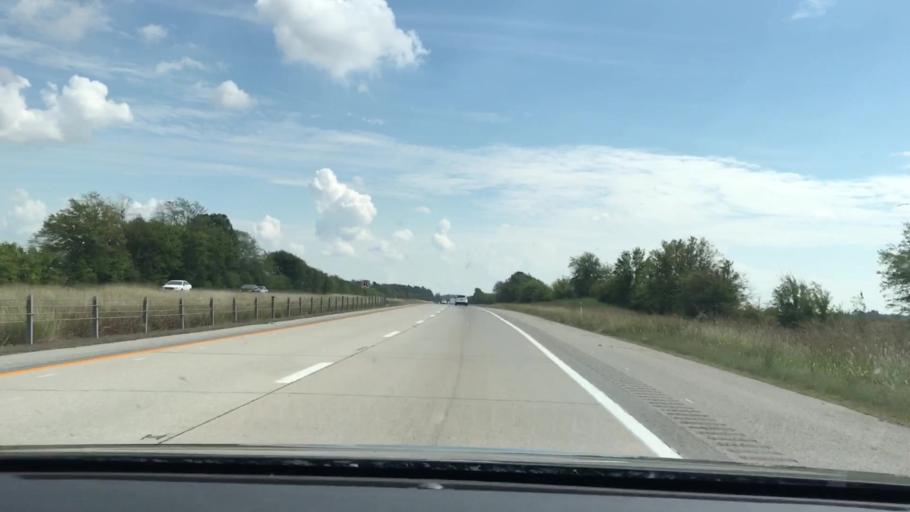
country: US
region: Kentucky
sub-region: Christian County
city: Hopkinsville
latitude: 36.7929
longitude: -87.5992
